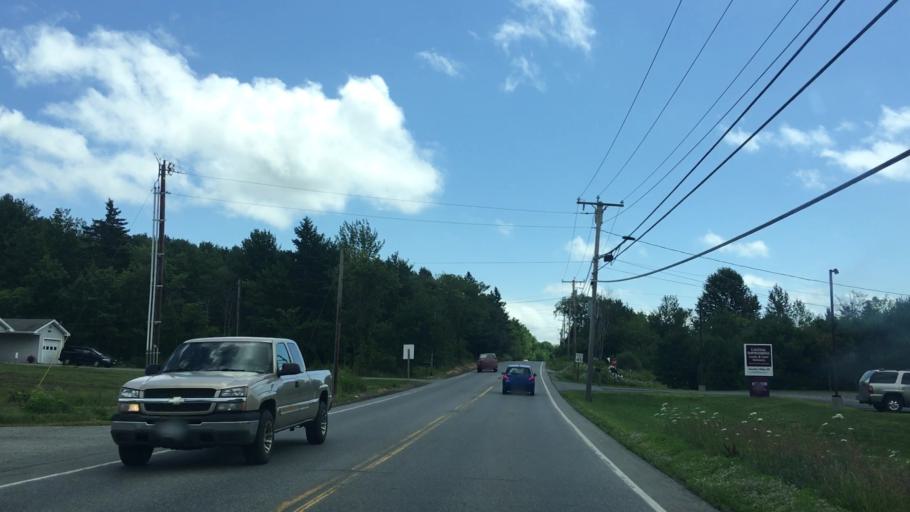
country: US
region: Maine
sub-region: Penobscot County
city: Hermon
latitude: 44.8046
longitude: -68.8997
